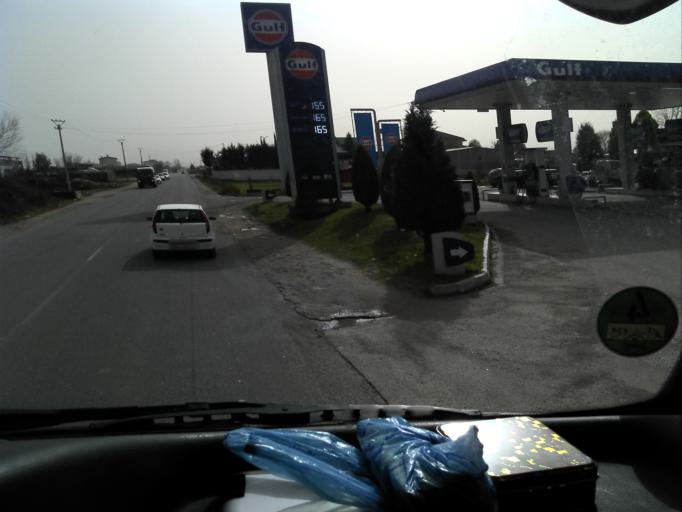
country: AL
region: Durres
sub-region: Rrethi i Krujes
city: Nikel
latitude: 41.4221
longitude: 19.7397
